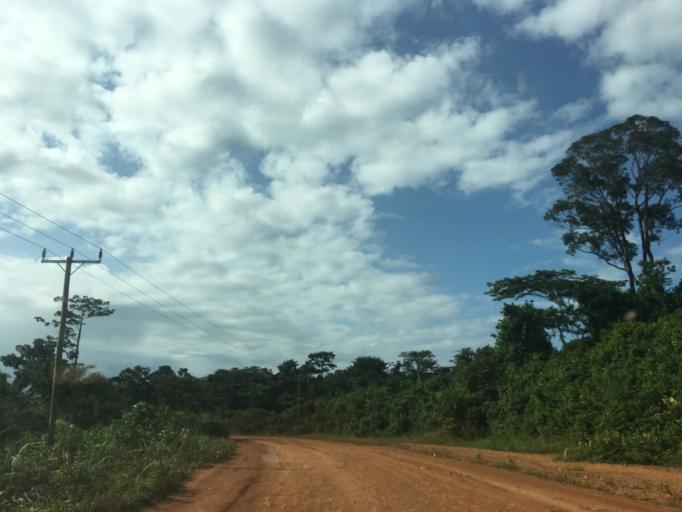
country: GH
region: Western
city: Wassa-Akropong
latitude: 5.9217
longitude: -2.4067
